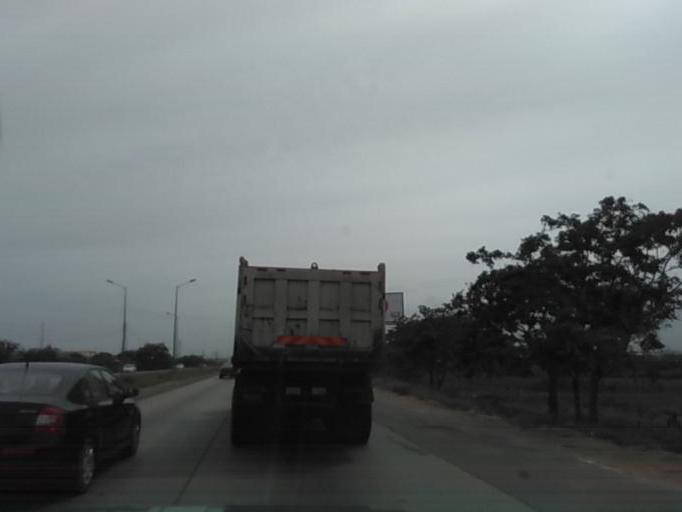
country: GH
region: Greater Accra
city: Tema
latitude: 5.6796
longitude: -0.0328
